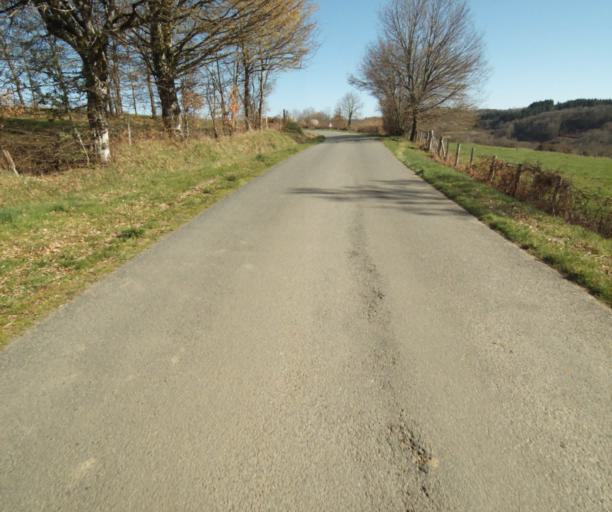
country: FR
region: Limousin
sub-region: Departement de la Correze
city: Chamboulive
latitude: 45.4243
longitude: 1.6440
